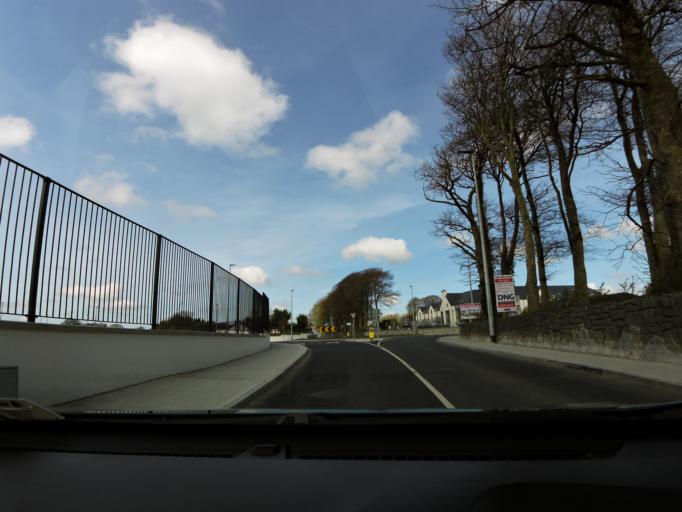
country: IE
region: Connaught
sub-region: County Galway
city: Athenry
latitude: 53.2995
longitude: -8.7604
